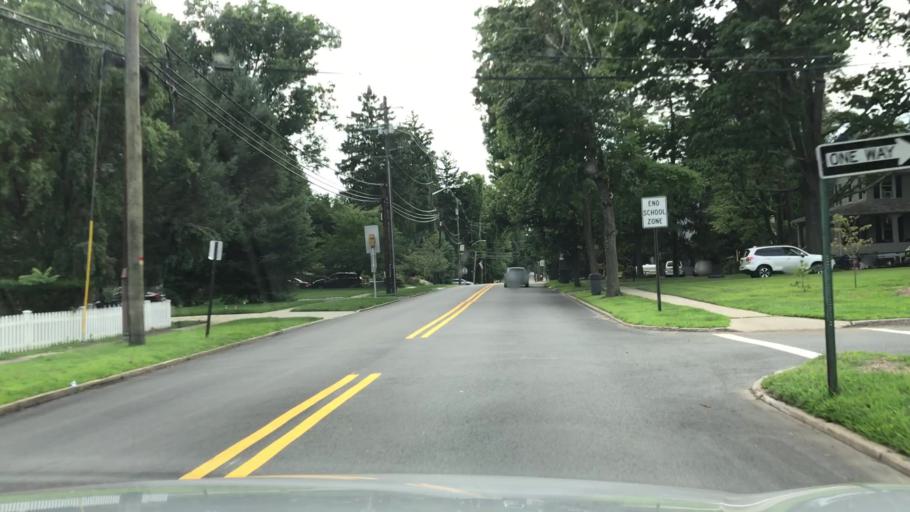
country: US
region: New Jersey
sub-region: Bergen County
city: Harrington Park
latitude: 40.9855
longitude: -73.9835
